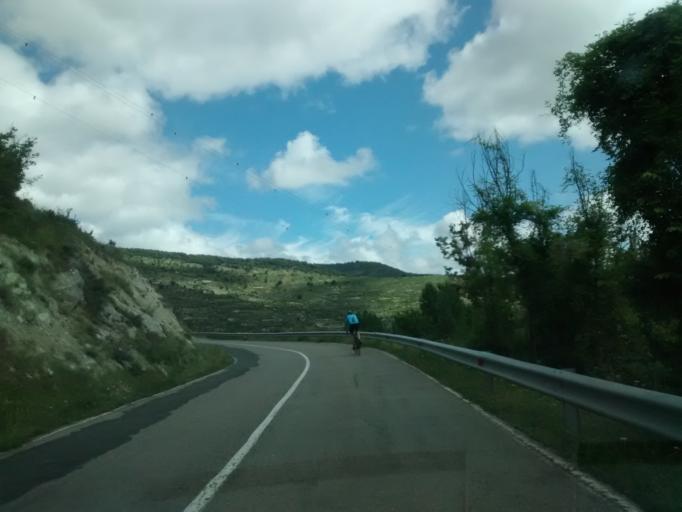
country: ES
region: La Rioja
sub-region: Provincia de La Rioja
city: Terroba
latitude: 42.2491
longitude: -2.4536
